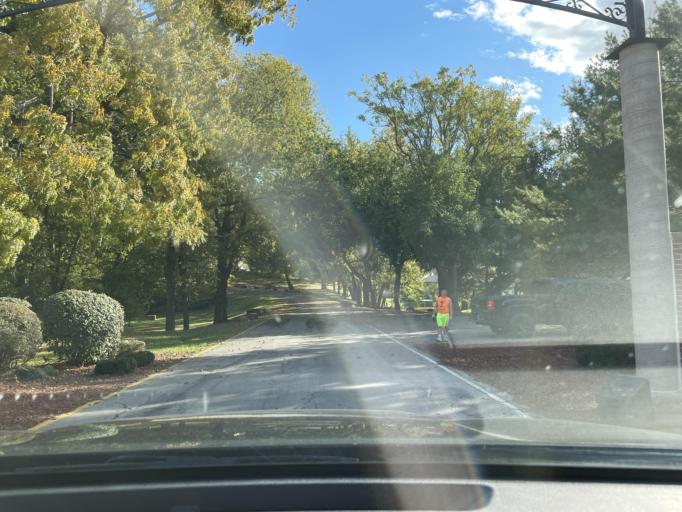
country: US
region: Kansas
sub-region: Doniphan County
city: Elwood
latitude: 39.7113
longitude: -94.8559
